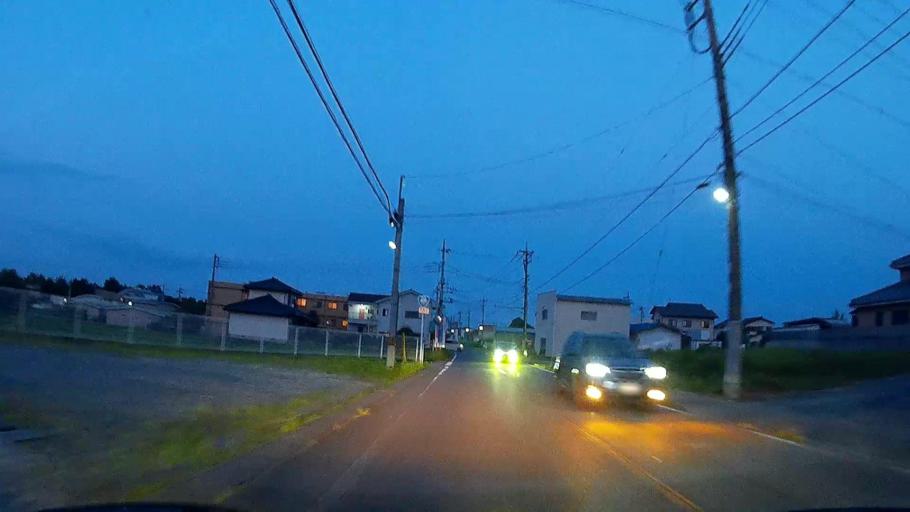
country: JP
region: Gunma
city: Takasaki
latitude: 36.3426
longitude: 138.9672
